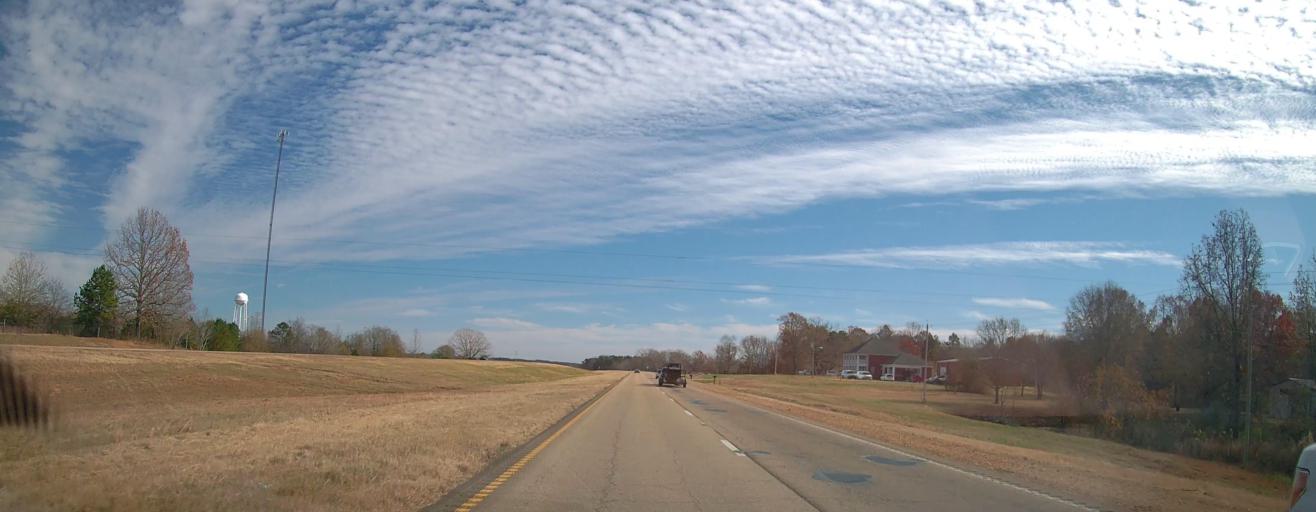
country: US
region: Mississippi
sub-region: Tippah County
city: Ripley
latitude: 34.9476
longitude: -88.8066
